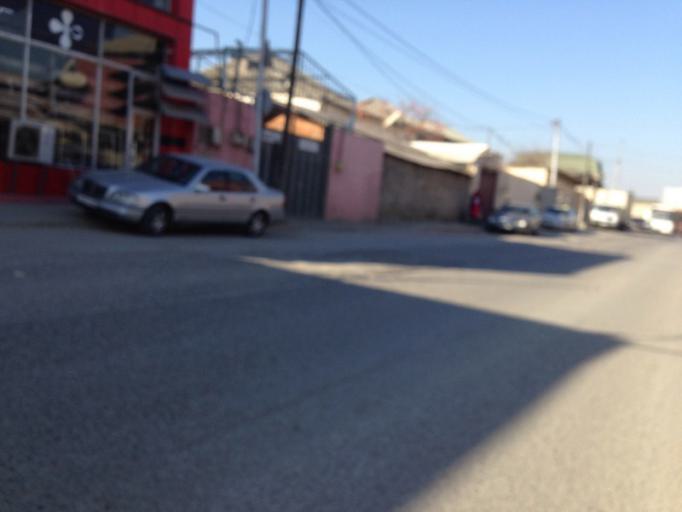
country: AZ
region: Baki
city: Baku
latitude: 40.4181
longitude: 49.8667
